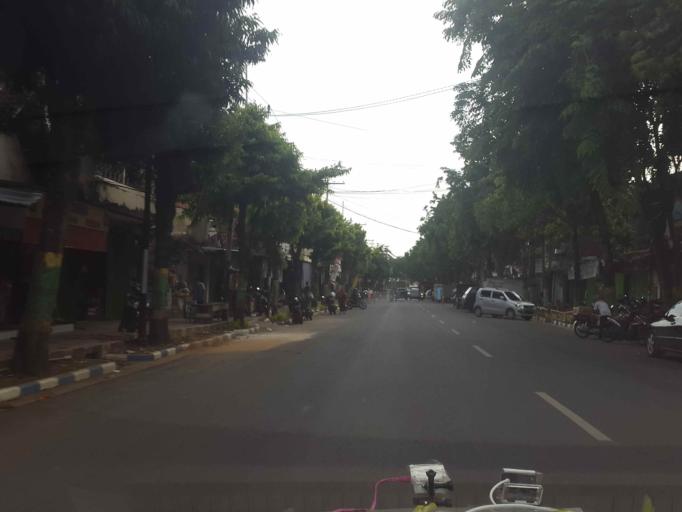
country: ID
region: East Java
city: Sumenep
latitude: -7.0042
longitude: 113.8606
